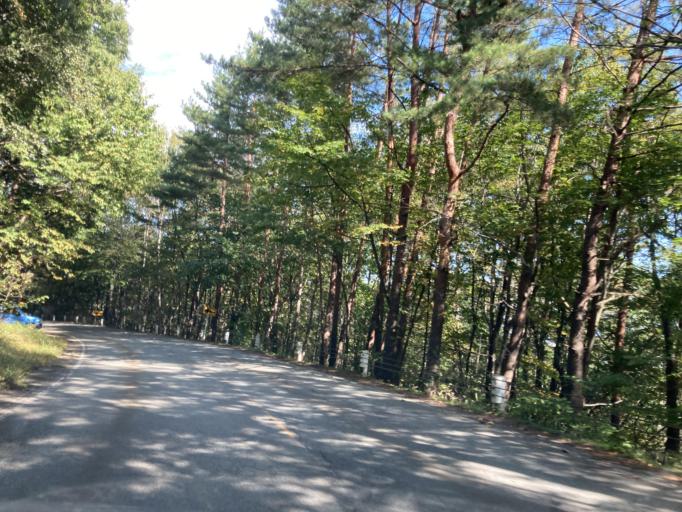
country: JP
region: Nagano
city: Omachi
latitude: 36.5215
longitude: 137.7891
